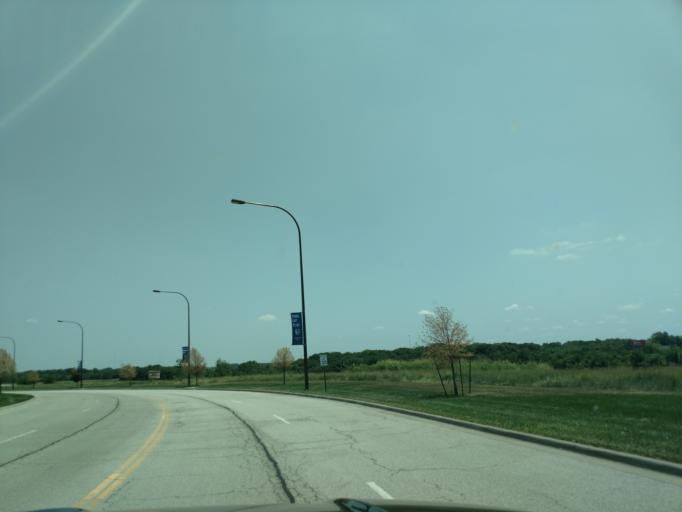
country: US
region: Kansas
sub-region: Wyandotte County
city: Edwardsville
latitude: 39.1093
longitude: -94.8286
